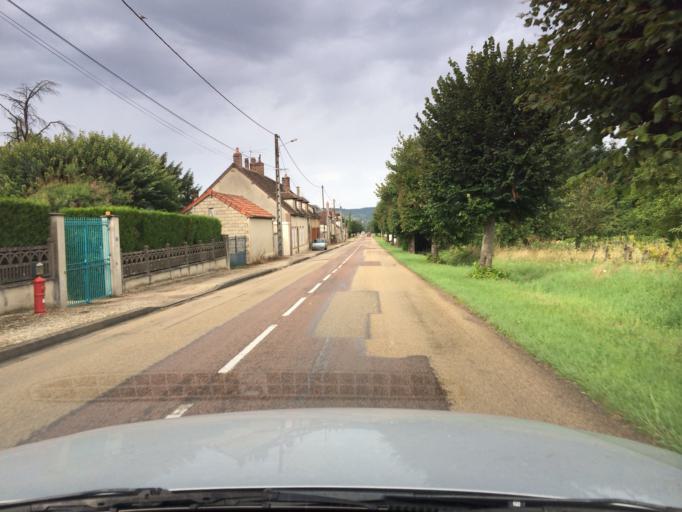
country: FR
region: Bourgogne
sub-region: Departement de l'Yonne
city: Joigny
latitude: 47.9532
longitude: 3.3741
